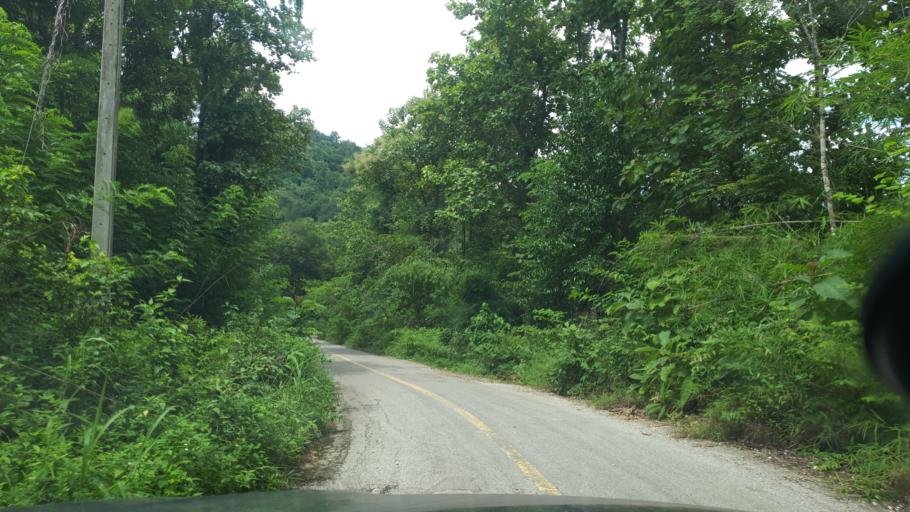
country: TH
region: Lampang
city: Hang Chat
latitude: 18.3566
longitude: 99.2548
